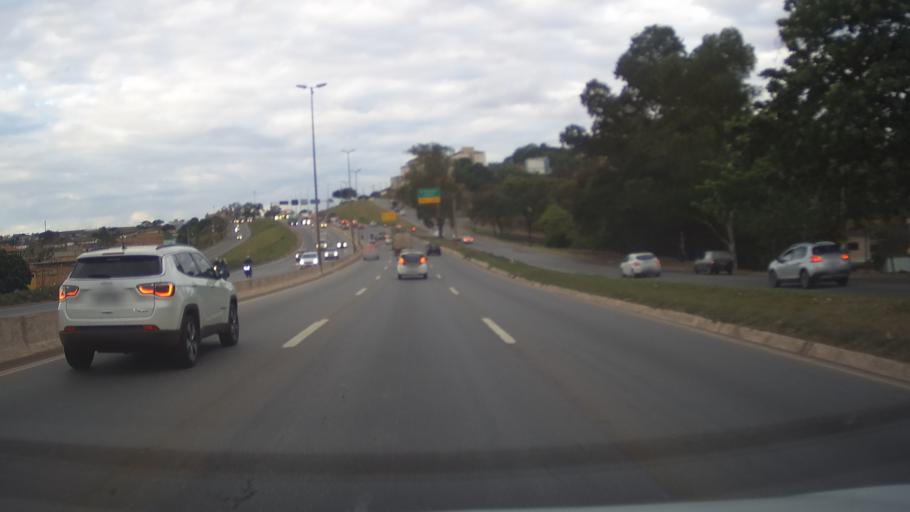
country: BR
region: Minas Gerais
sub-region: Contagem
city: Contagem
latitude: -19.9188
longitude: -43.9979
